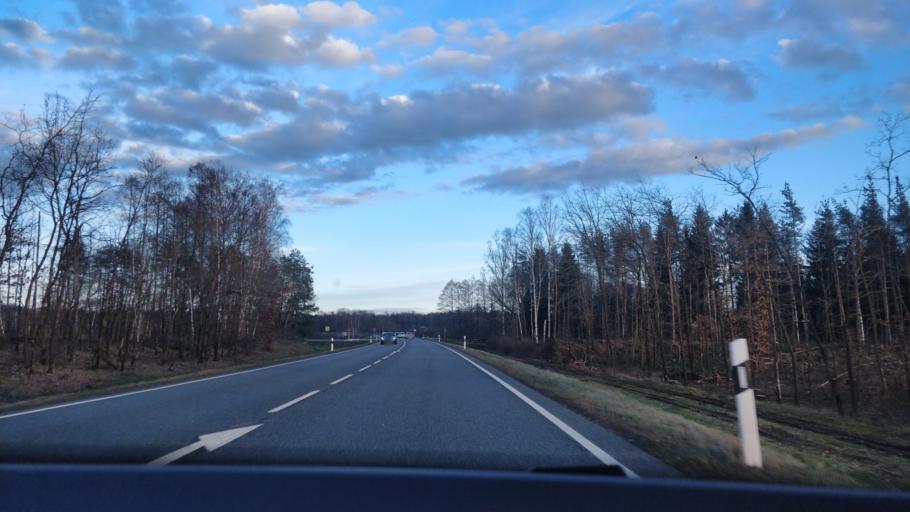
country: DE
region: Bavaria
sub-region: Upper Palatinate
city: Schwarzenbach
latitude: 49.7213
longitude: 11.9770
